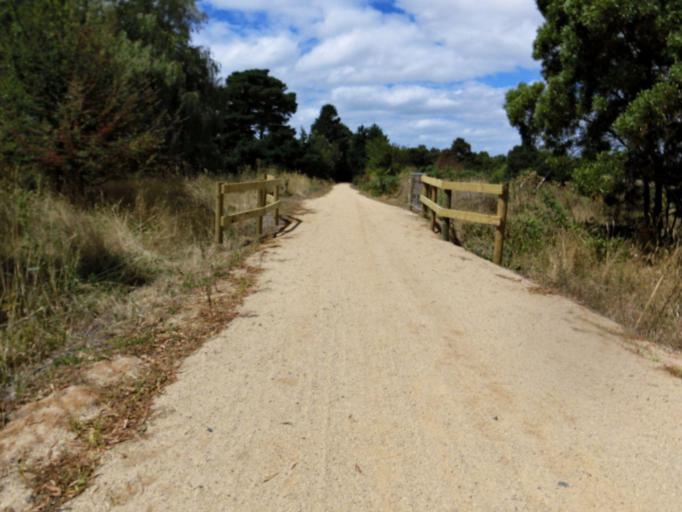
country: AU
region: Victoria
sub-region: Bass Coast
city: North Wonthaggi
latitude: -38.4125
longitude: 145.7712
